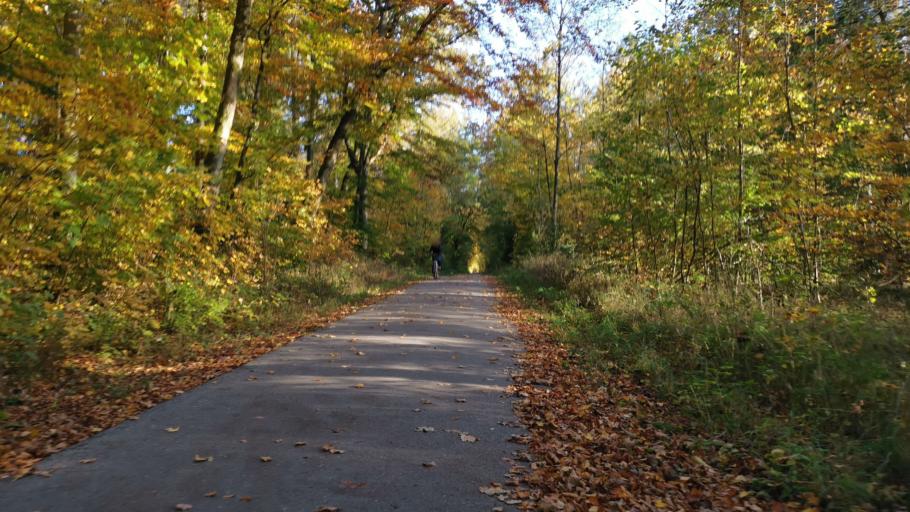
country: DE
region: Bavaria
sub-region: Upper Bavaria
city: Pullach im Isartal
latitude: 48.0697
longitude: 11.5500
